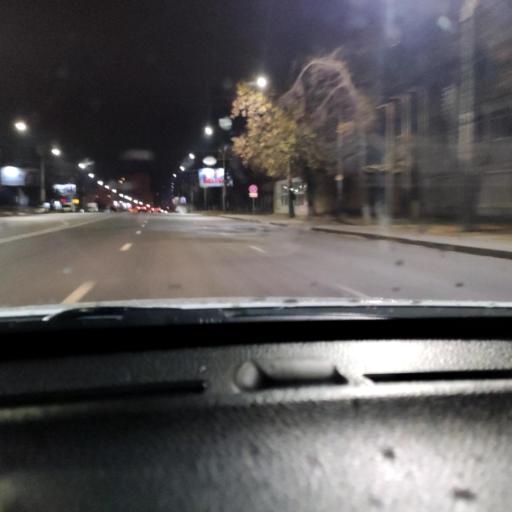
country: RU
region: Voronezj
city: Voronezh
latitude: 51.6456
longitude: 39.1986
